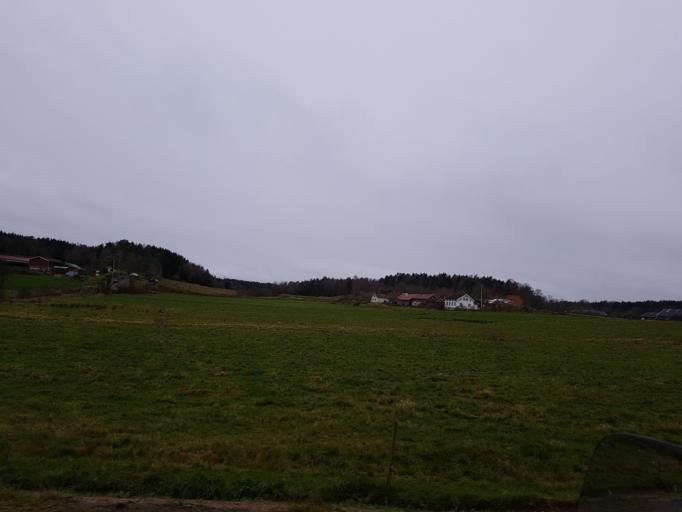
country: SE
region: Vaestra Goetaland
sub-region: Orust
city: Henan
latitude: 58.2475
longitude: 11.7249
